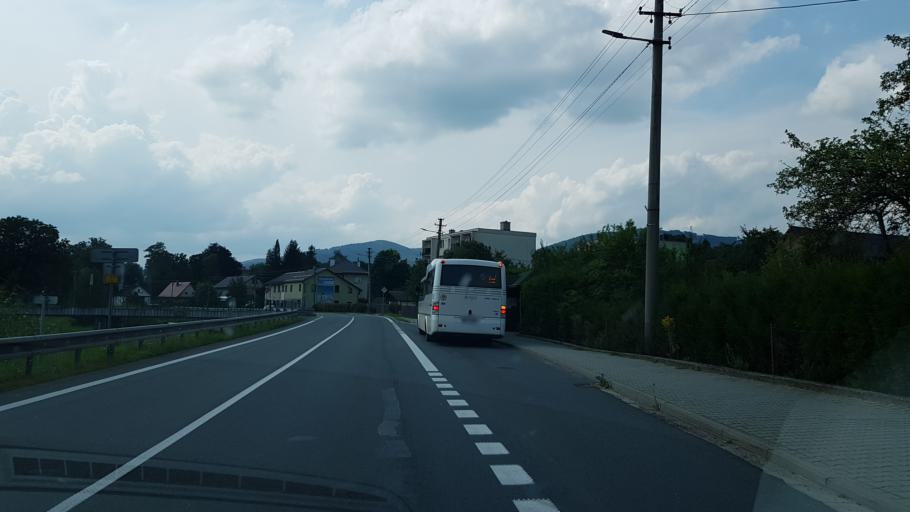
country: CZ
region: Olomoucky
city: Pisecna
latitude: 50.2727
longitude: 17.2509
